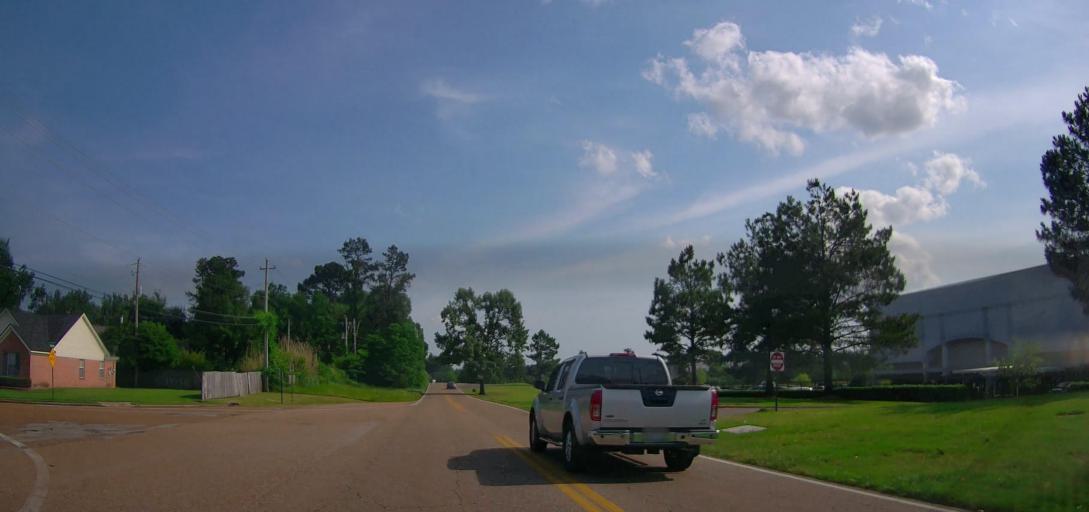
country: US
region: Mississippi
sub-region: De Soto County
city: Olive Branch
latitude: 35.0116
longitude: -89.8489
